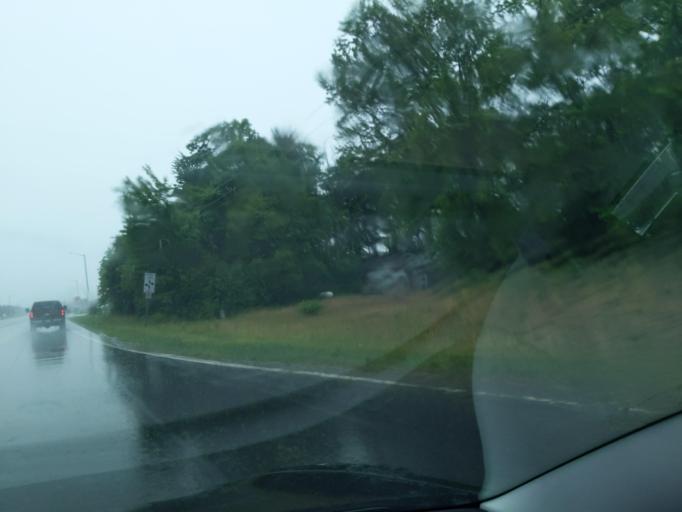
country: US
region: Michigan
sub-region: Muskegon County
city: Fruitport
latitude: 43.1542
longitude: -86.1959
